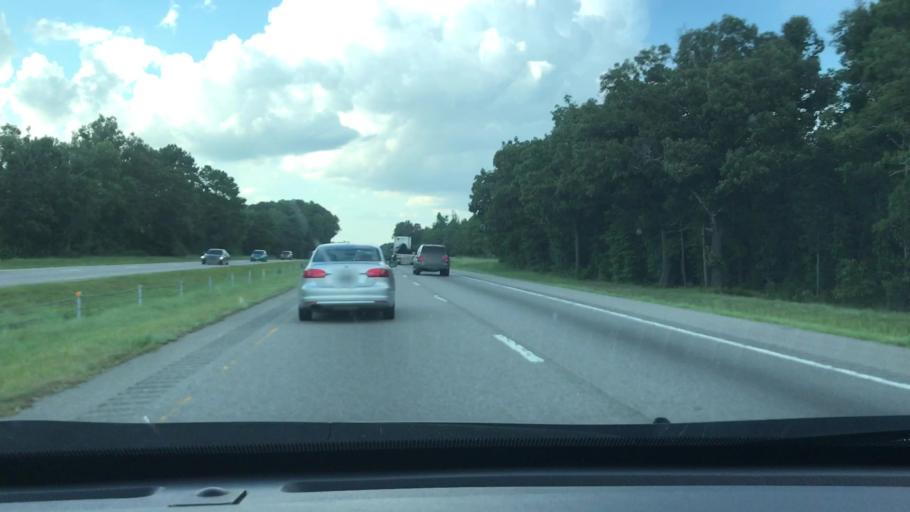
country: US
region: North Carolina
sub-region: Robeson County
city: Saint Pauls
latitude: 34.8708
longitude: -78.9634
